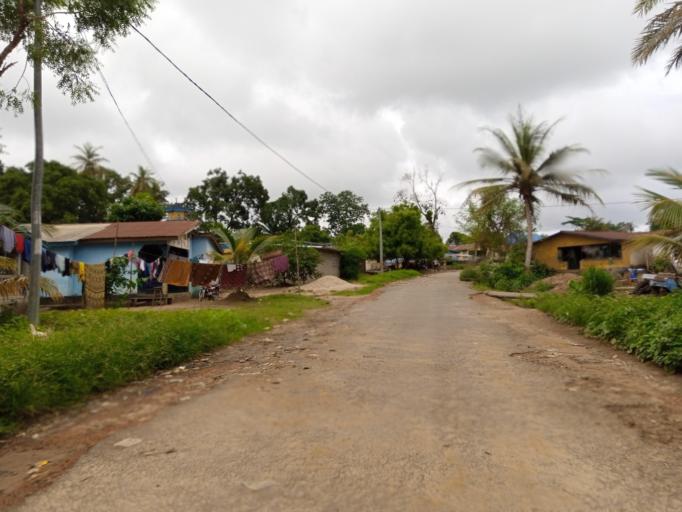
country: SL
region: Northern Province
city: Masoyila
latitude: 8.5963
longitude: -13.1957
